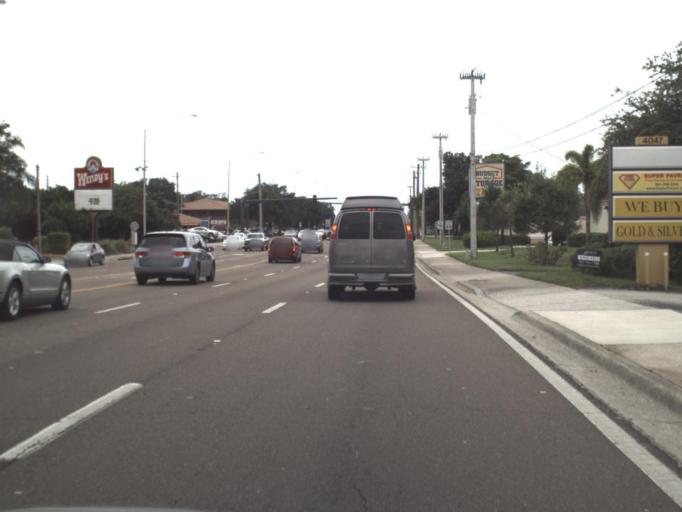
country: US
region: Florida
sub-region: Sarasota County
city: Sarasota Springs
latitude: 27.2989
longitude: -82.4874
